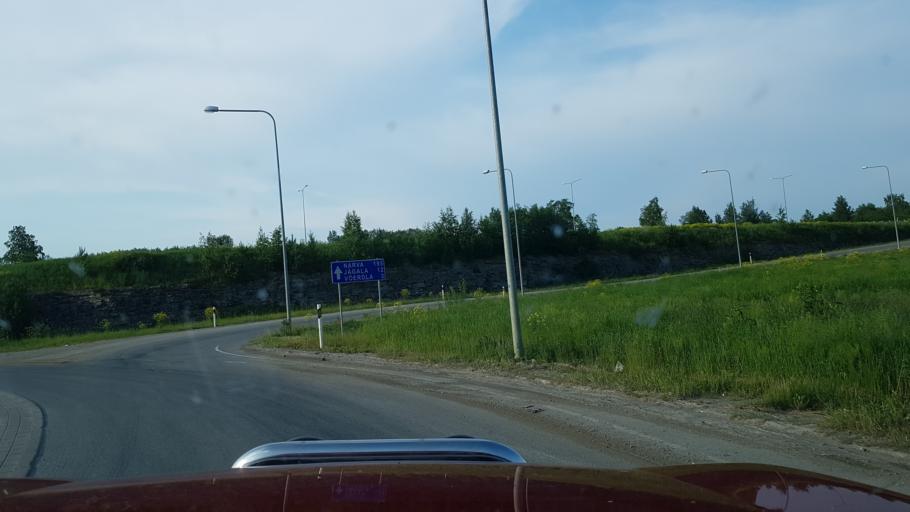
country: EE
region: Harju
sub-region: Maardu linn
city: Maardu
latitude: 59.4510
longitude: 25.0310
